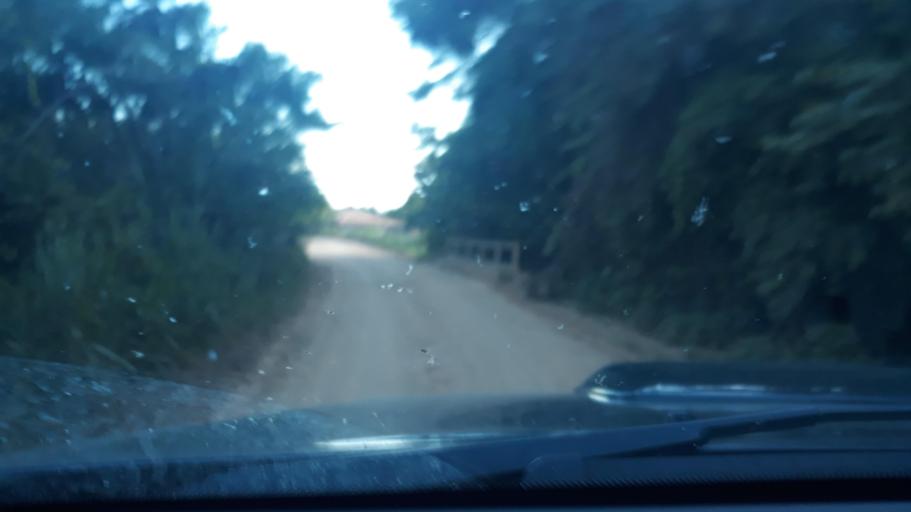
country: BR
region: Bahia
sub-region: Riacho De Santana
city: Riacho de Santana
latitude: -13.8302
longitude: -42.7301
